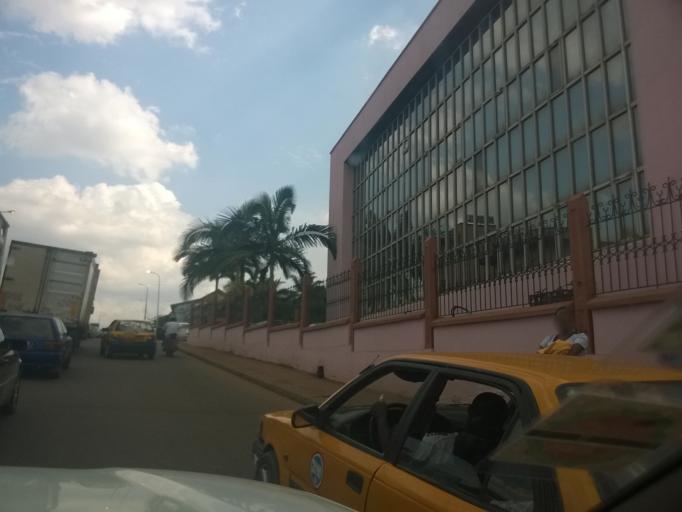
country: CM
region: Centre
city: Yaounde
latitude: 3.8559
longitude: 11.5205
